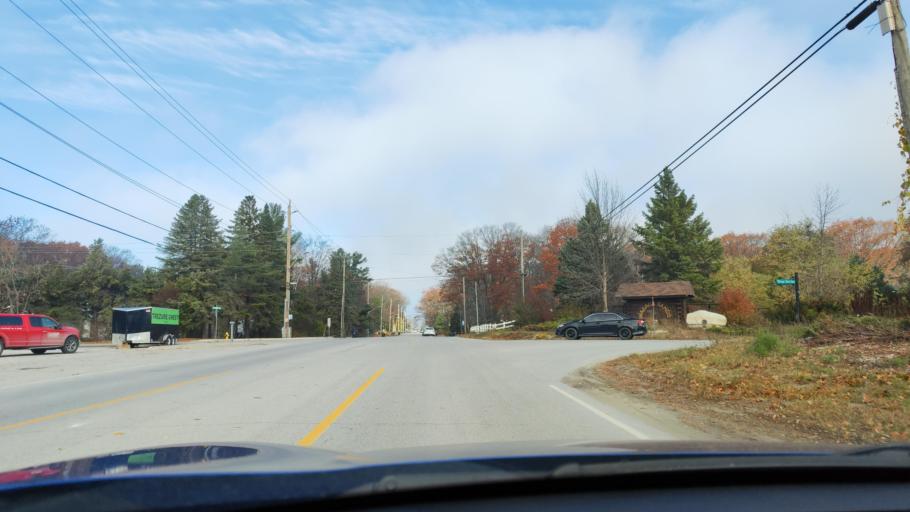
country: CA
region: Ontario
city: Wasaga Beach
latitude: 44.4635
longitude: -80.0735
